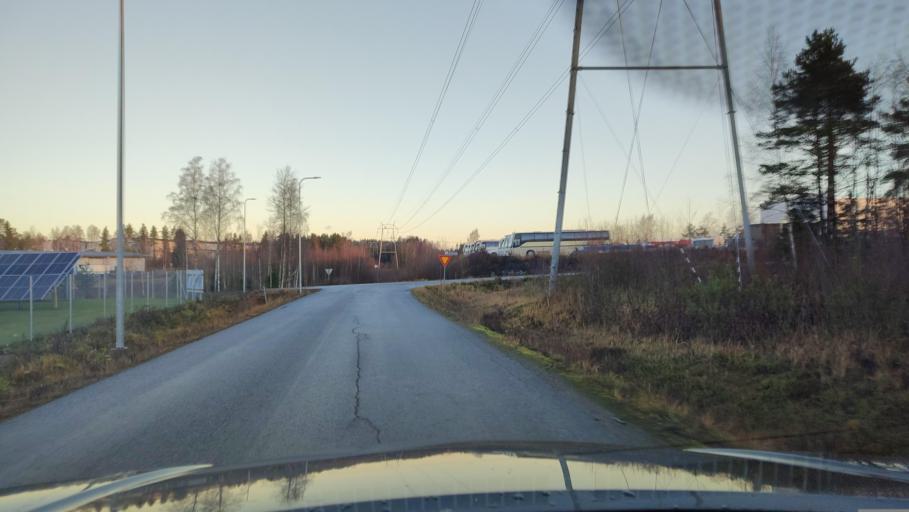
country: FI
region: Ostrobothnia
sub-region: Sydosterbotten
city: Naerpes
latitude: 62.4765
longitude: 21.3790
